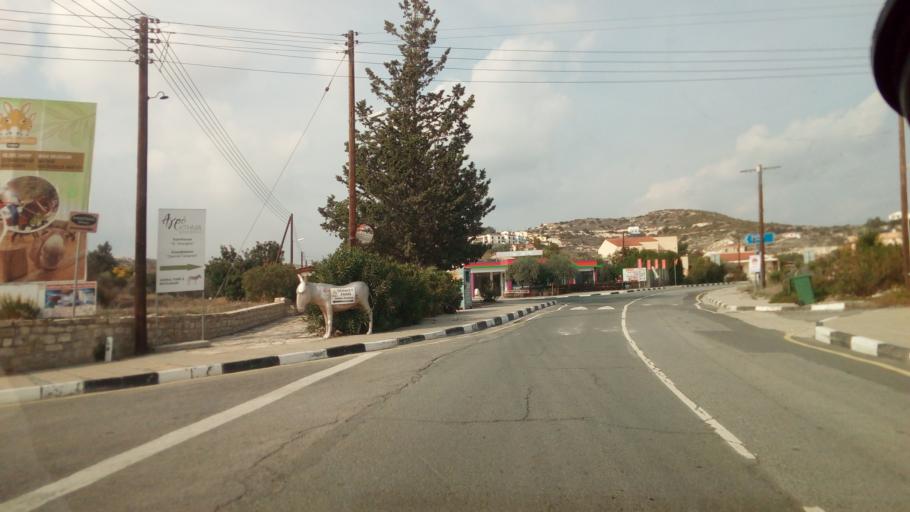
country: CY
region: Larnaka
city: Kofinou
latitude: 34.8192
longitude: 33.3587
